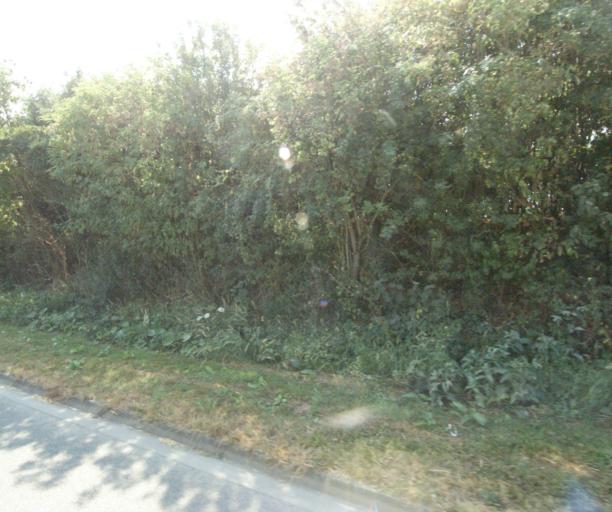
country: FR
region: Nord-Pas-de-Calais
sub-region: Departement du Nord
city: Comines
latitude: 50.7524
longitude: 3.0168
